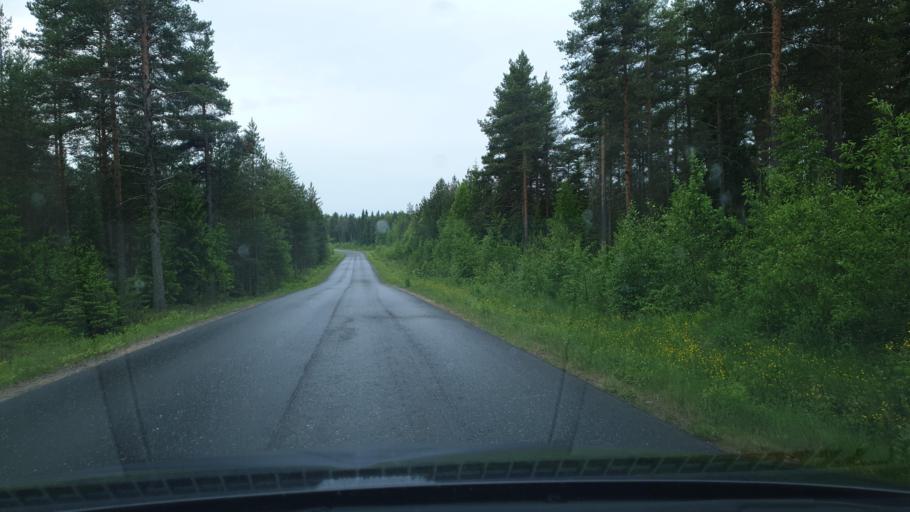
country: FI
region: Northern Ostrobothnia
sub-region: Oulunkaari
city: Ii
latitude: 65.2981
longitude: 25.3832
